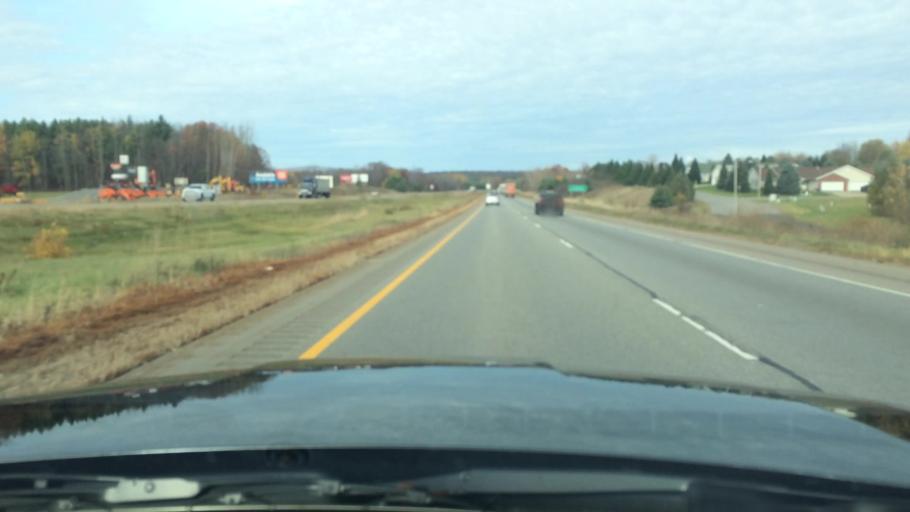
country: US
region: Wisconsin
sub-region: Marathon County
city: Mosinee
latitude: 44.7958
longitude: -89.6793
